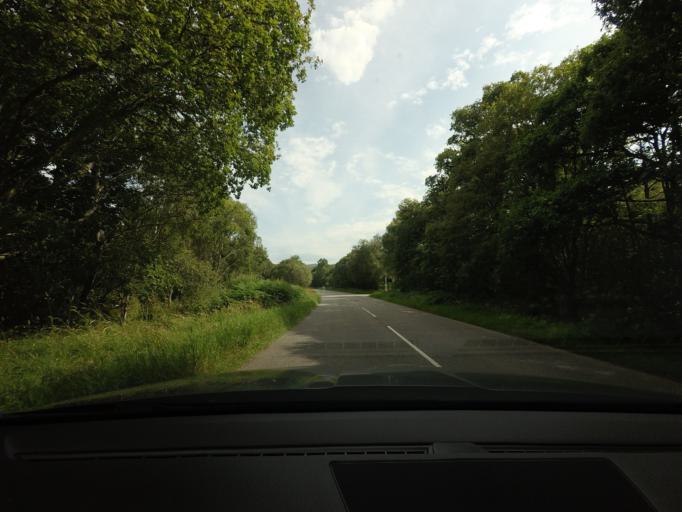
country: GB
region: Scotland
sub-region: Highland
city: Alness
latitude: 57.8765
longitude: -4.3579
